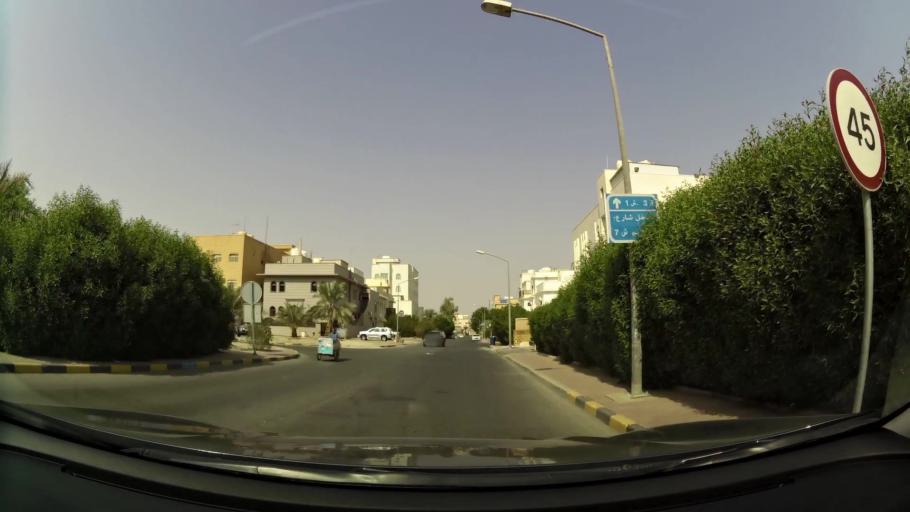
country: KW
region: Muhafazat al Jahra'
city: Al Jahra'
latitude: 29.3316
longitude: 47.6514
